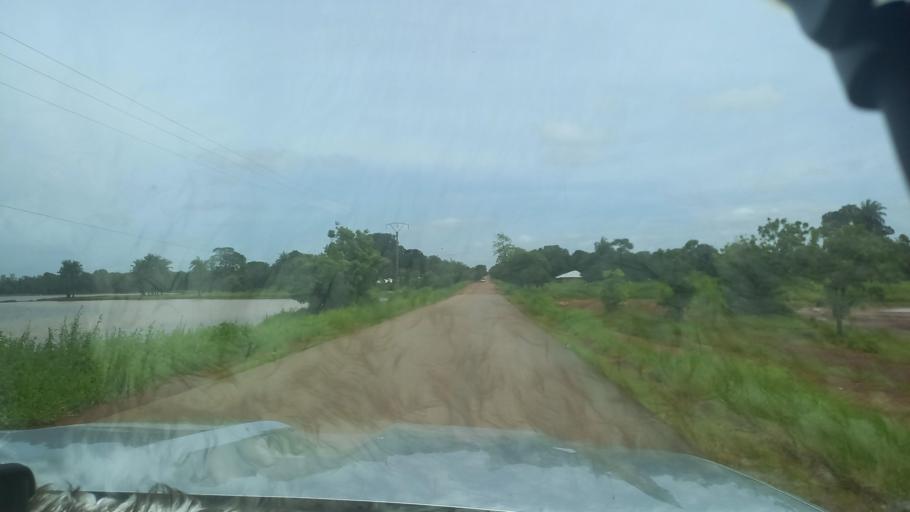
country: SN
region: Kolda
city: Marsassoum
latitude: 12.9660
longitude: -15.9644
